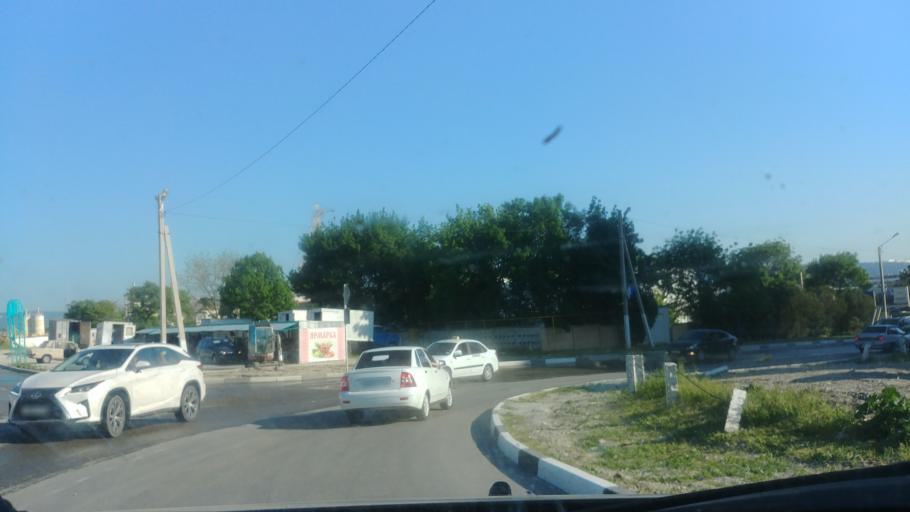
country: RU
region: Krasnodarskiy
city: Gelendzhik
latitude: 44.5717
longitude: 38.0928
